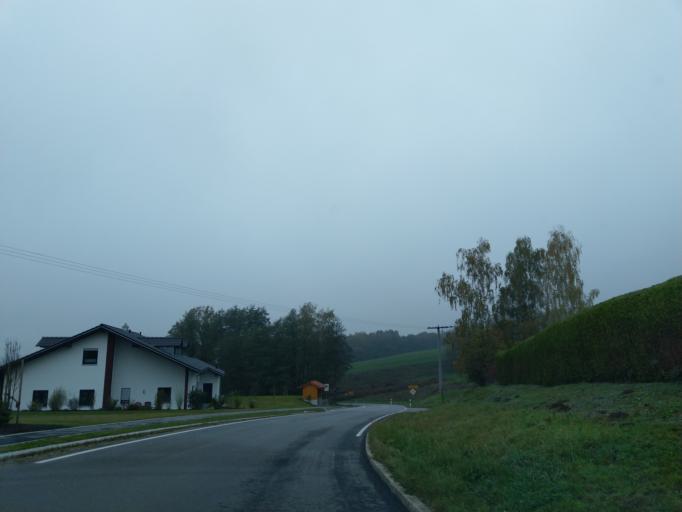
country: DE
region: Bavaria
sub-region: Lower Bavaria
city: Grattersdorf
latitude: 48.7901
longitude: 13.1404
